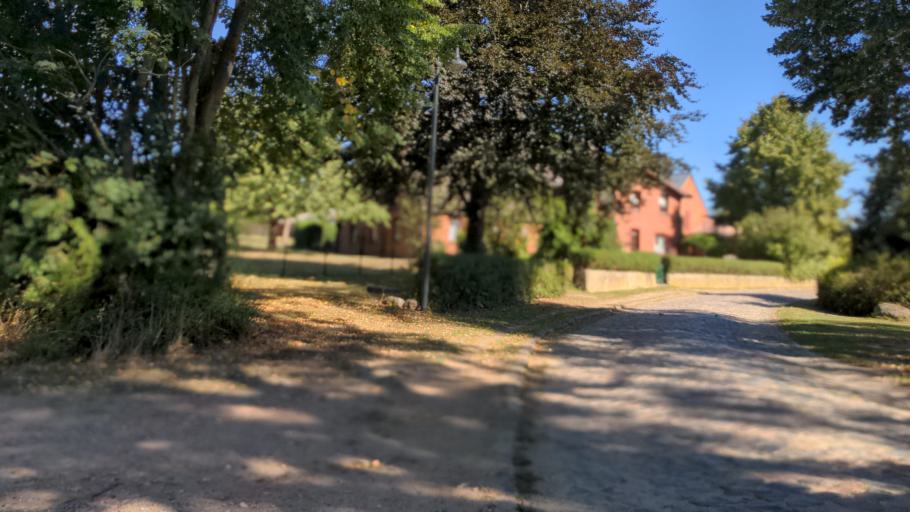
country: DE
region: Schleswig-Holstein
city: Gross Disnack
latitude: 53.7439
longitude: 10.6921
